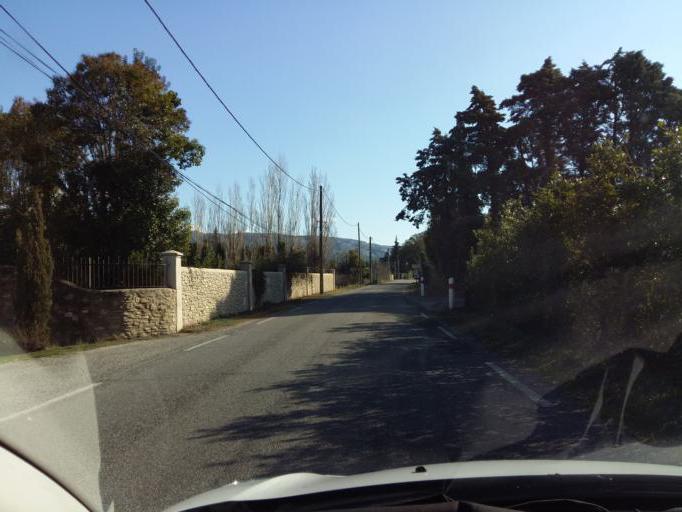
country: FR
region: Provence-Alpes-Cote d'Azur
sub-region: Departement du Vaucluse
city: Cheval-Blanc
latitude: 43.8111
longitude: 5.0619
